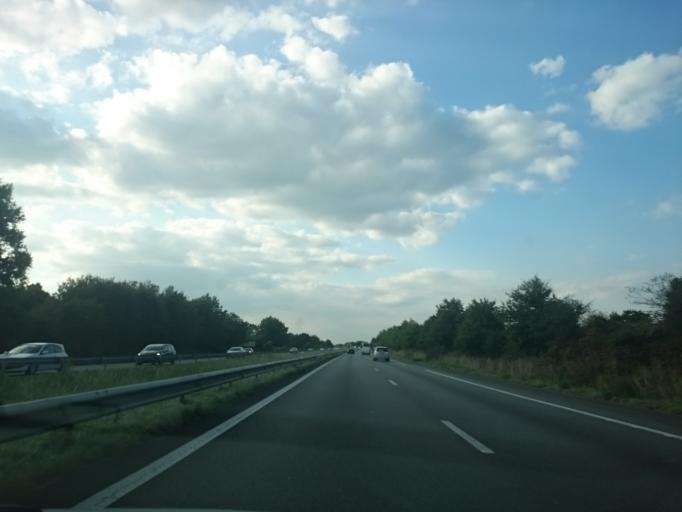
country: FR
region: Pays de la Loire
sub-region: Departement de la Loire-Atlantique
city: Sautron
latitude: 47.2704
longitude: -1.7148
